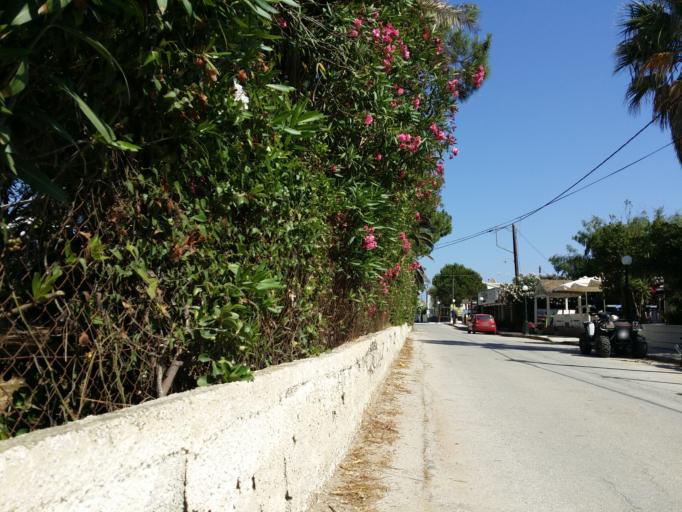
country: GR
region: Ionian Islands
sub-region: Nomos Kerkyras
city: Perivoli
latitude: 39.4282
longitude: 19.9418
